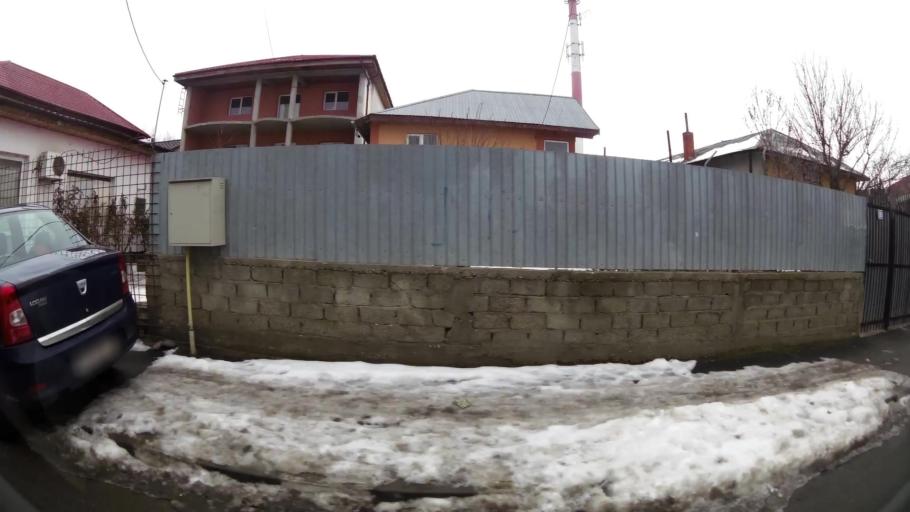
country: RO
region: Ilfov
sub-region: Comuna Pantelimon
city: Pantelimon
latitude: 44.4591
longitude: 26.2044
